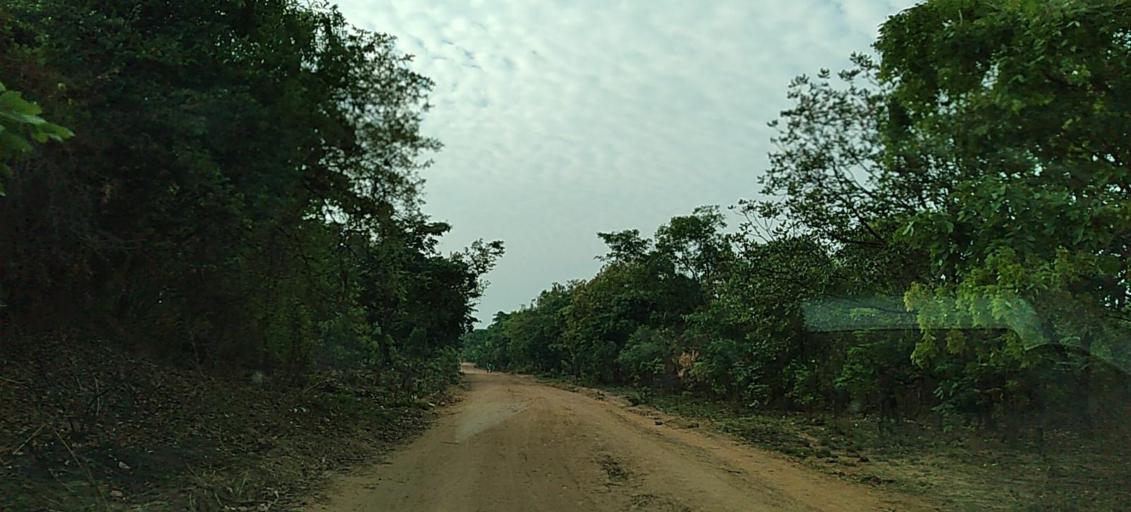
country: ZM
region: Copperbelt
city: Kalulushi
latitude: -12.9048
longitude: 27.6874
